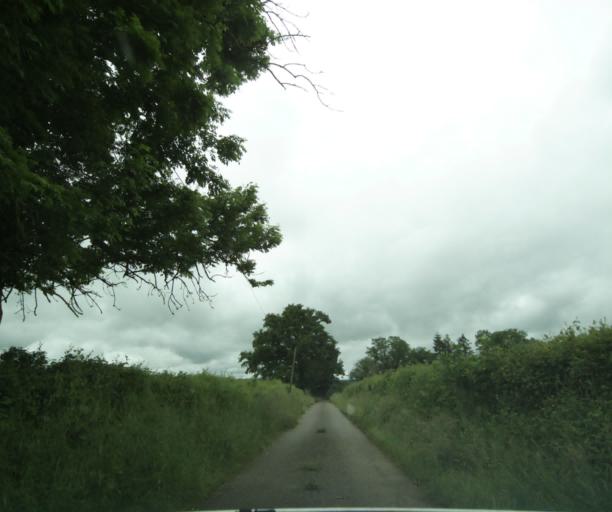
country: FR
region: Bourgogne
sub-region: Departement de Saone-et-Loire
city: Charolles
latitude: 46.4698
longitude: 4.3509
